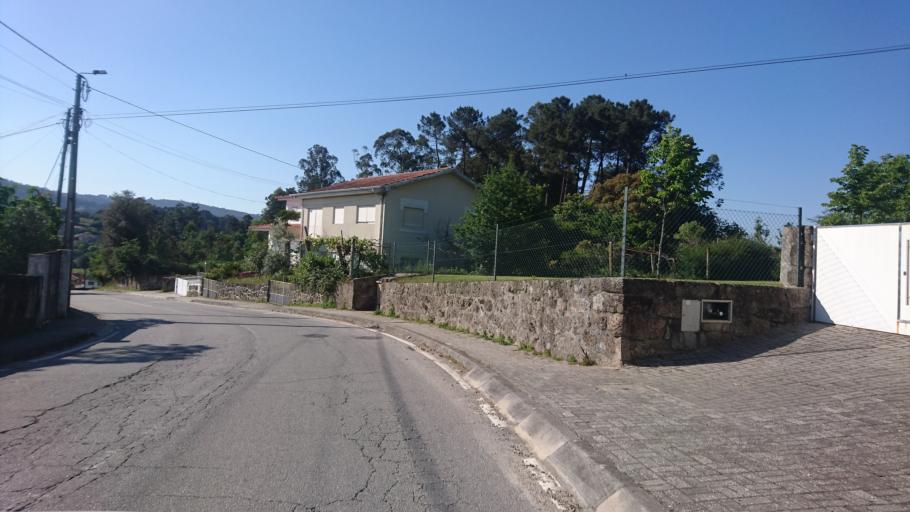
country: PT
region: Porto
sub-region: Paredes
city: Casteloes de Cepeda
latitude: 41.1901
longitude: -8.3314
